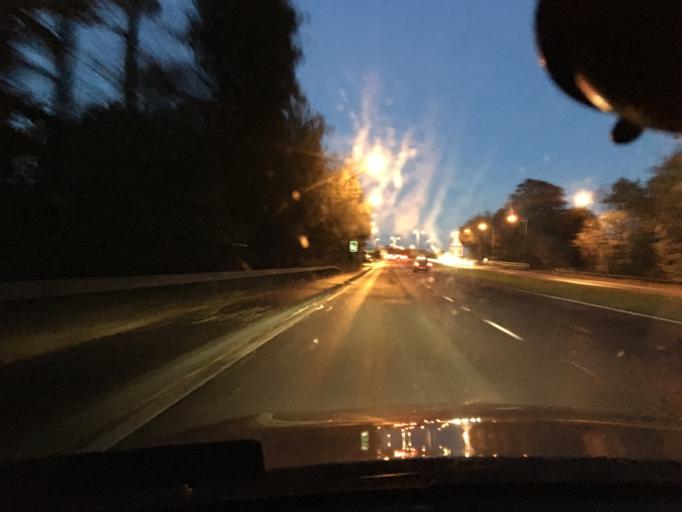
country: GB
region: Northern Ireland
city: Hillsborough
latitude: 54.4863
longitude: -6.0664
